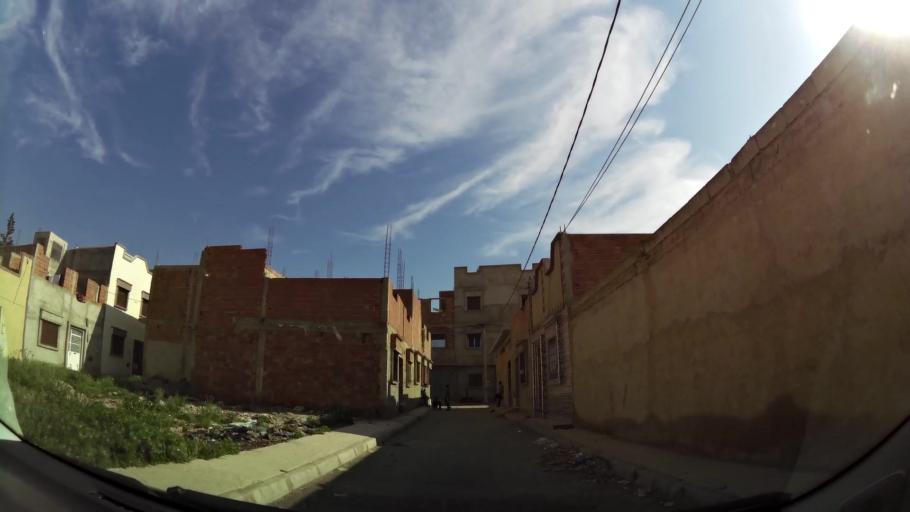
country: MA
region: Oriental
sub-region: Oujda-Angad
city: Oujda
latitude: 34.7217
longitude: -1.8857
